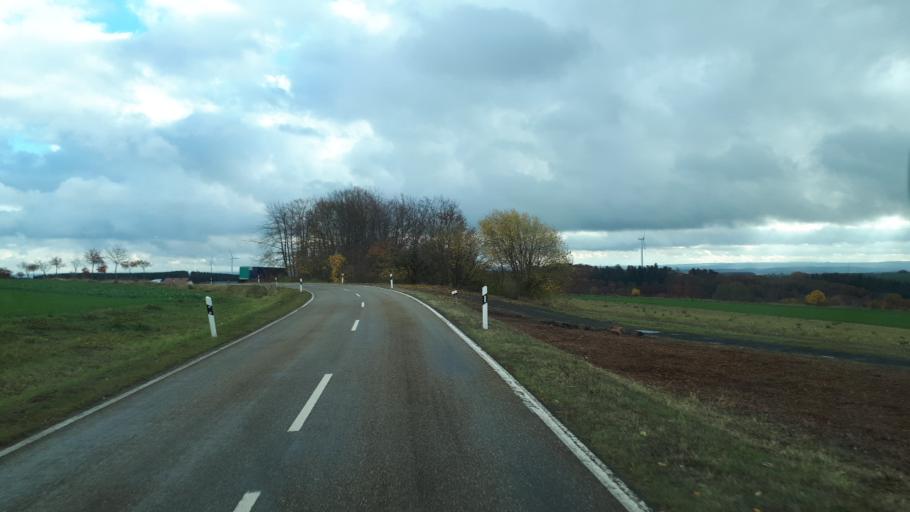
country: DE
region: Rheinland-Pfalz
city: Eulgem
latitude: 50.2261
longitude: 7.1711
